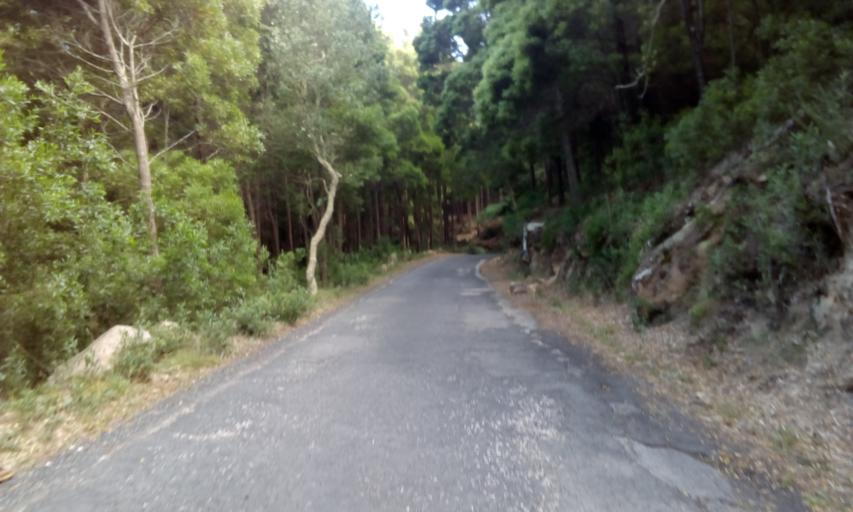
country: PT
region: Lisbon
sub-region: Sintra
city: Colares
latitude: 38.7754
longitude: -9.4369
